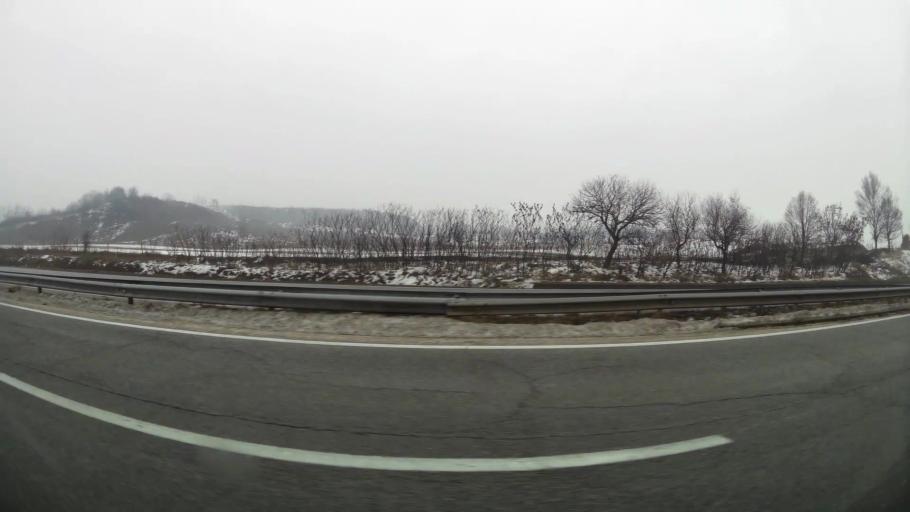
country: MK
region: Petrovec
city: Petrovec
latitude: 41.9418
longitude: 21.6286
